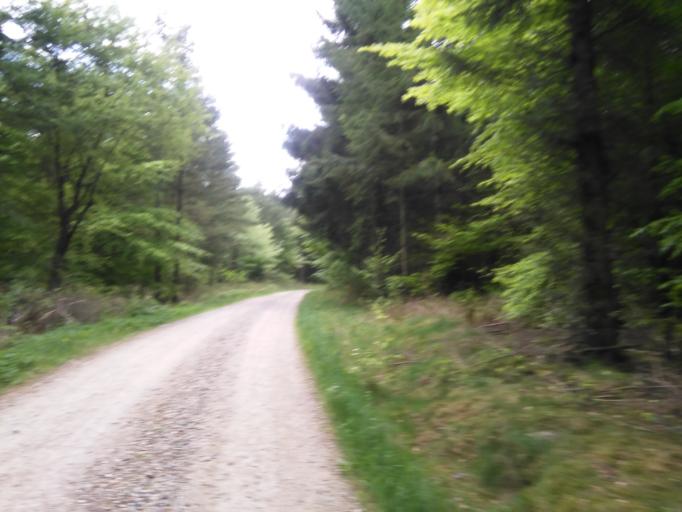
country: DK
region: Central Jutland
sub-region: Horsens Kommune
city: Braedstrup
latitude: 56.0498
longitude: 9.6122
